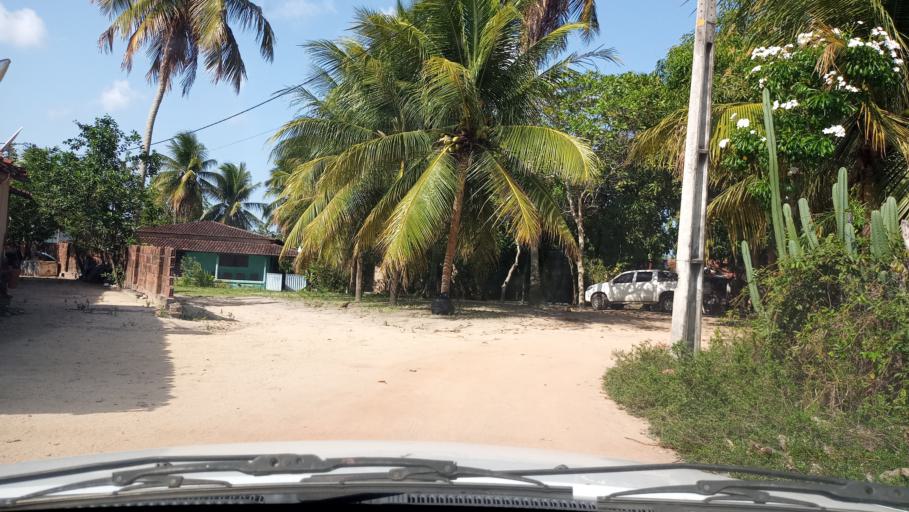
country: BR
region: Rio Grande do Norte
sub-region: Ares
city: Ares
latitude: -6.2231
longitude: -35.1498
